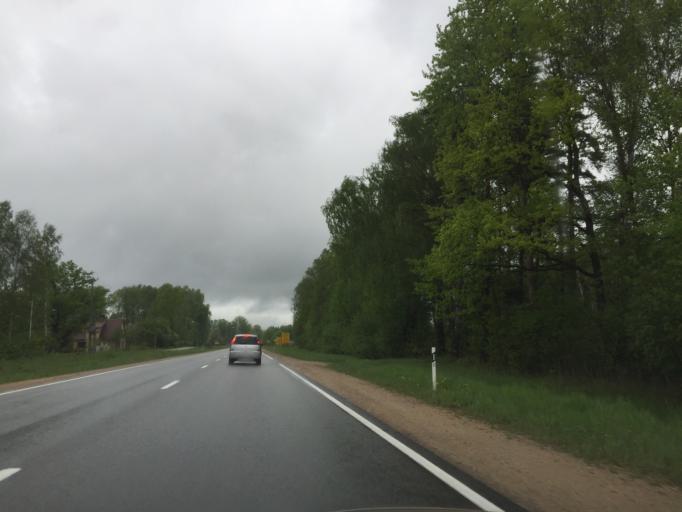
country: LV
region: Kegums
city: Kegums
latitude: 56.7368
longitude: 24.7308
